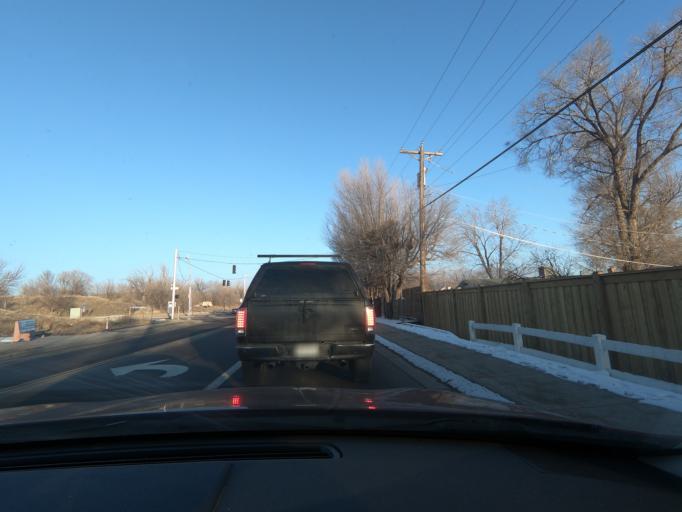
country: US
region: Colorado
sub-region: El Paso County
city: Security-Widefield
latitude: 38.7373
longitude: -104.7197
